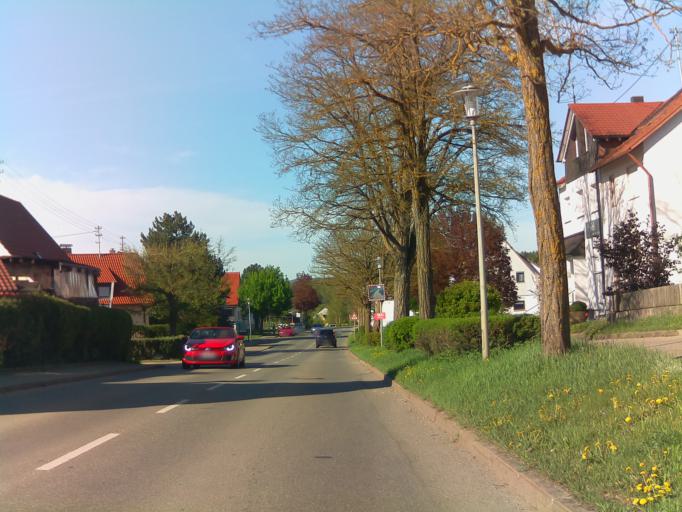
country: DE
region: Baden-Wuerttemberg
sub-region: Freiburg Region
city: Dietingen
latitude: 48.2030
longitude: 8.6476
